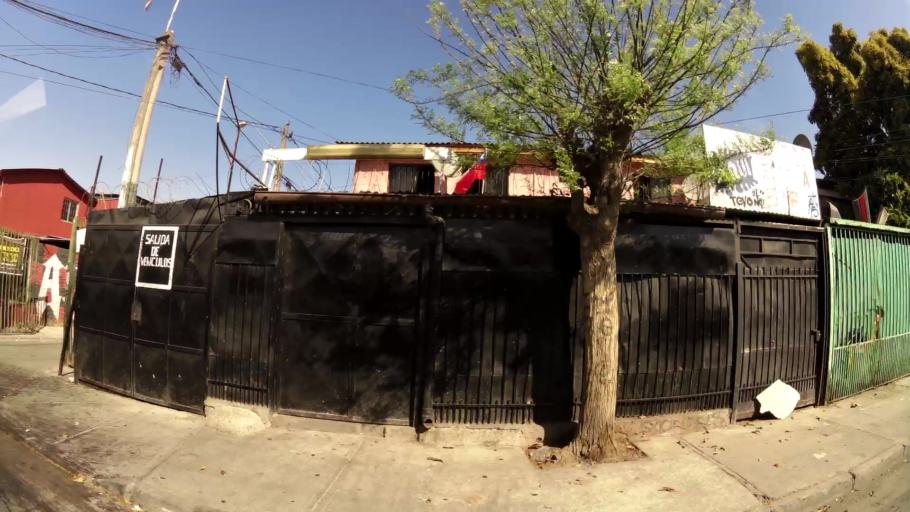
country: CL
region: Santiago Metropolitan
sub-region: Provincia de Santiago
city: La Pintana
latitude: -33.5590
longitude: -70.6207
